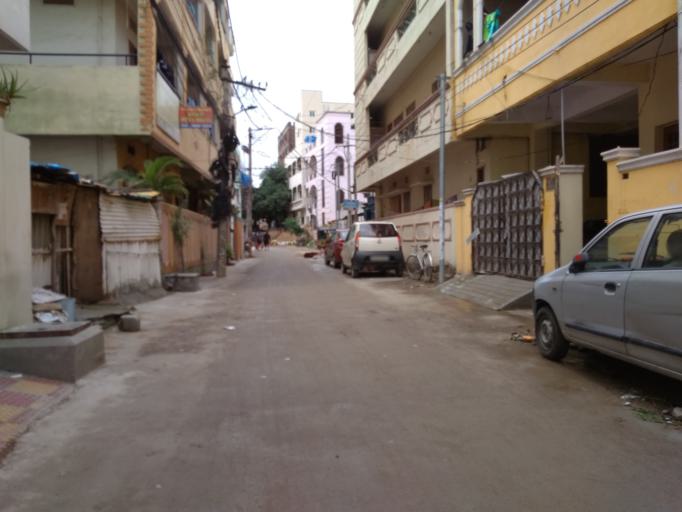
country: IN
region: Telangana
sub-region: Rangareddi
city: Kukatpalli
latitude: 17.4436
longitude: 78.3608
